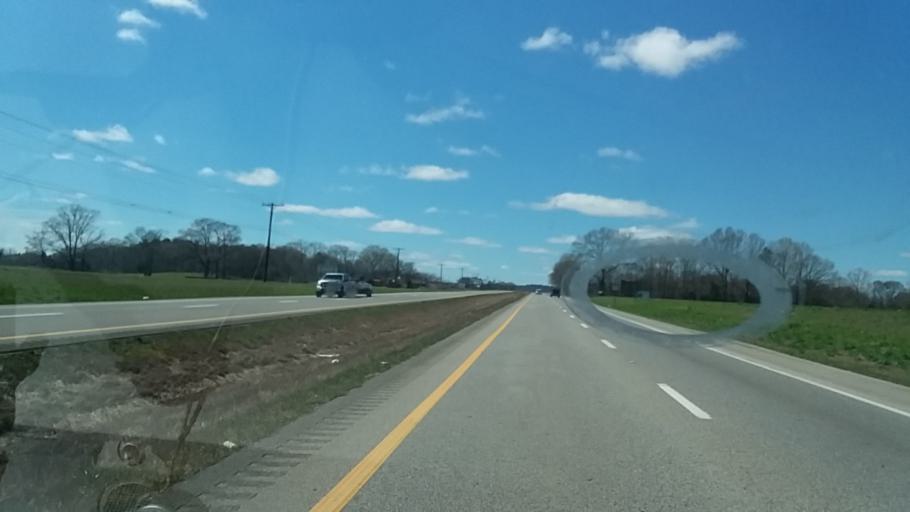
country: US
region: Alabama
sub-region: Colbert County
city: Tuscumbia
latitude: 34.7112
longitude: -87.7265
